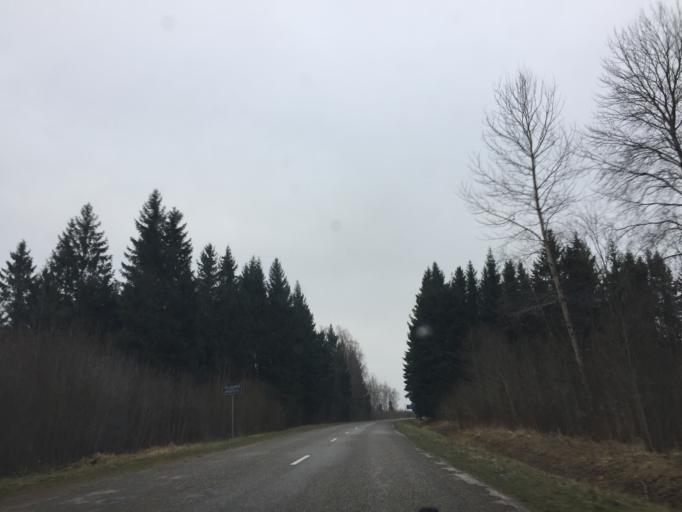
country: LV
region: Limbazu Rajons
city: Limbazi
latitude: 57.5805
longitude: 24.6613
